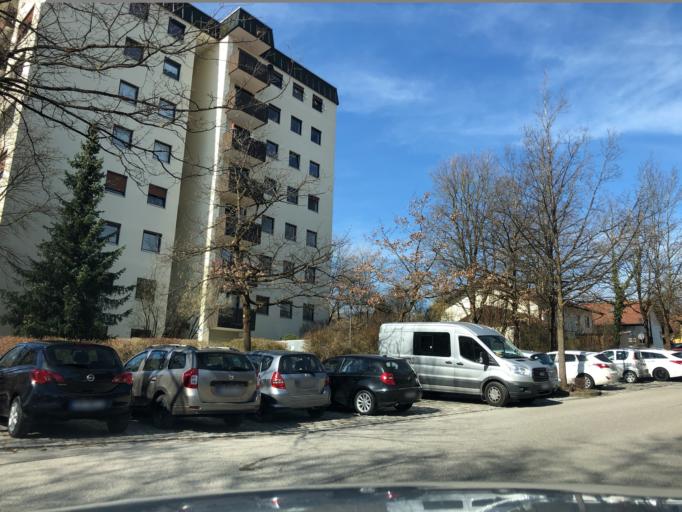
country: DE
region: Bavaria
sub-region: Upper Bavaria
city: Ebersberg
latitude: 48.0742
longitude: 11.9562
